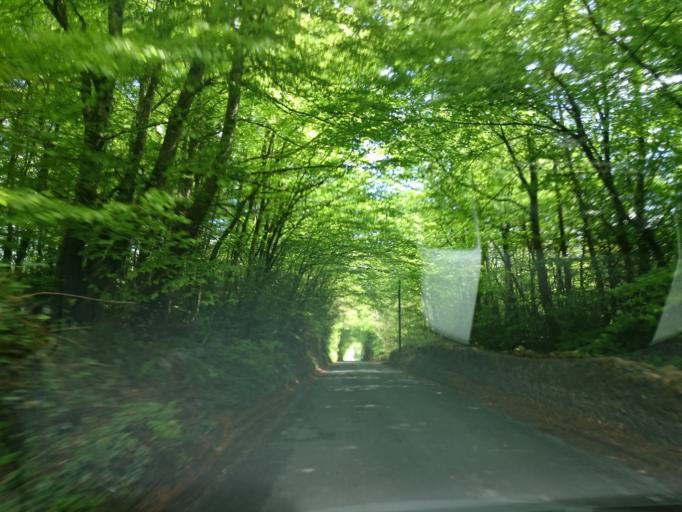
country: IE
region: Leinster
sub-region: Laois
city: Mountrath
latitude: 53.0320
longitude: -7.5520
